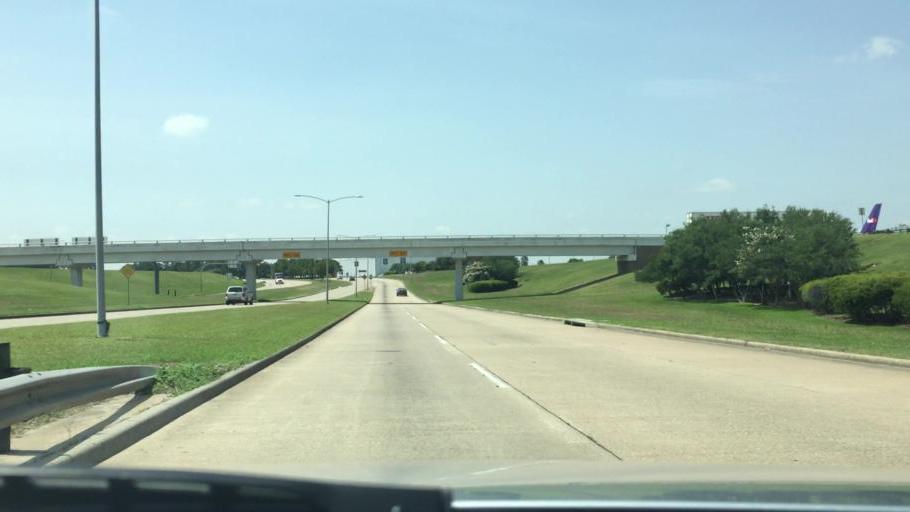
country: US
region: Texas
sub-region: Harris County
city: Aldine
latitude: 29.9796
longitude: -95.3430
